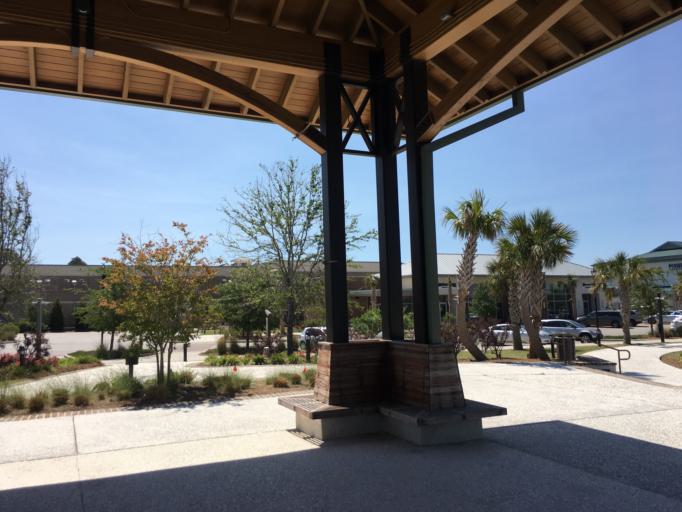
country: US
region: South Carolina
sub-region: Beaufort County
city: Hilton Head Island
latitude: 32.1869
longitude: -80.7209
